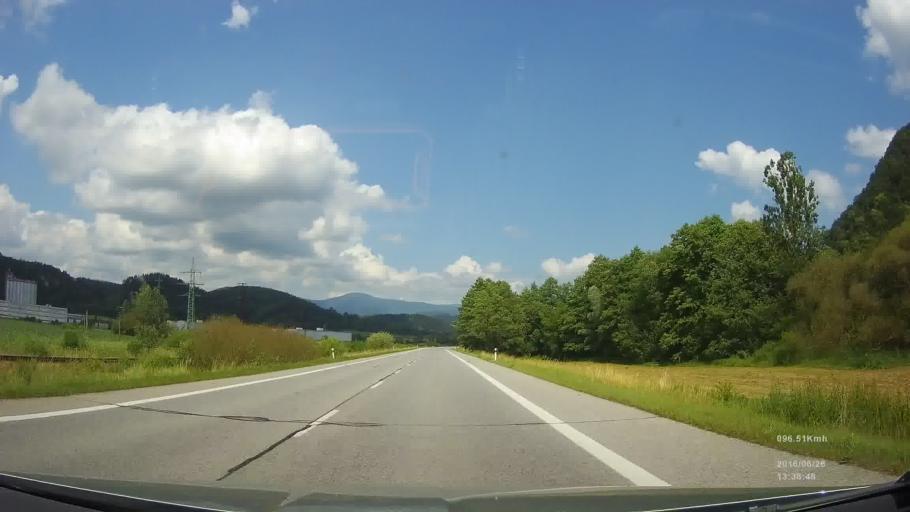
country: SK
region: Banskobystricky
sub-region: Okres Banska Bystrica
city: Banska Bystrica
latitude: 48.7504
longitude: 19.2544
